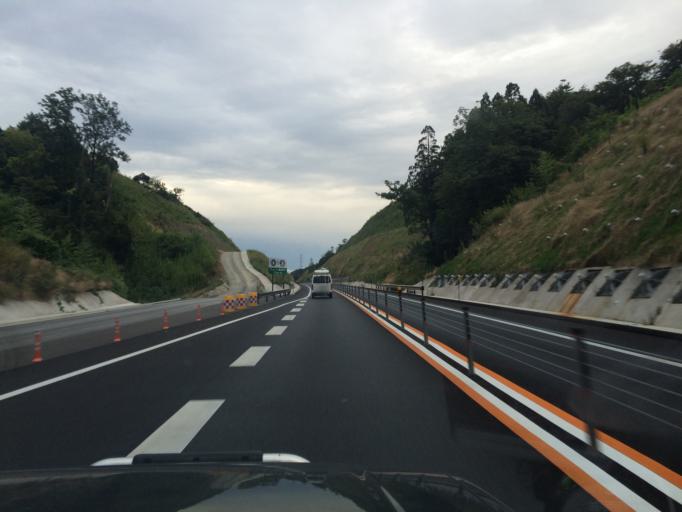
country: JP
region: Tottori
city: Tottori
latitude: 35.4927
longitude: 134.1394
